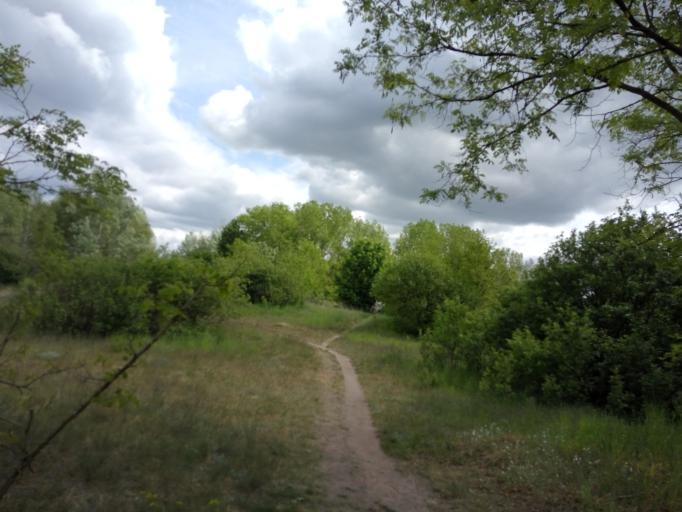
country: DE
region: Berlin
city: Kaulsdorf
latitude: 52.4906
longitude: 13.5899
